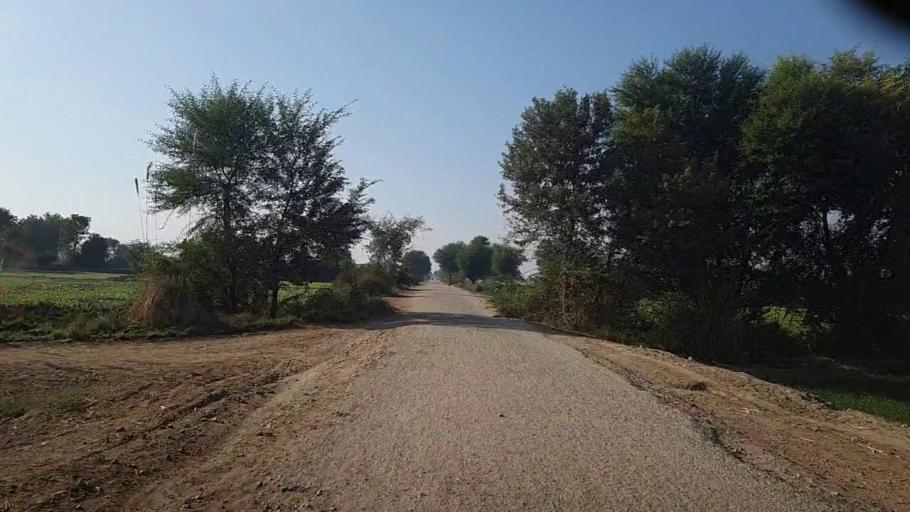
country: PK
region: Sindh
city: Darya Khan Marri
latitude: 26.6821
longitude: 68.3637
